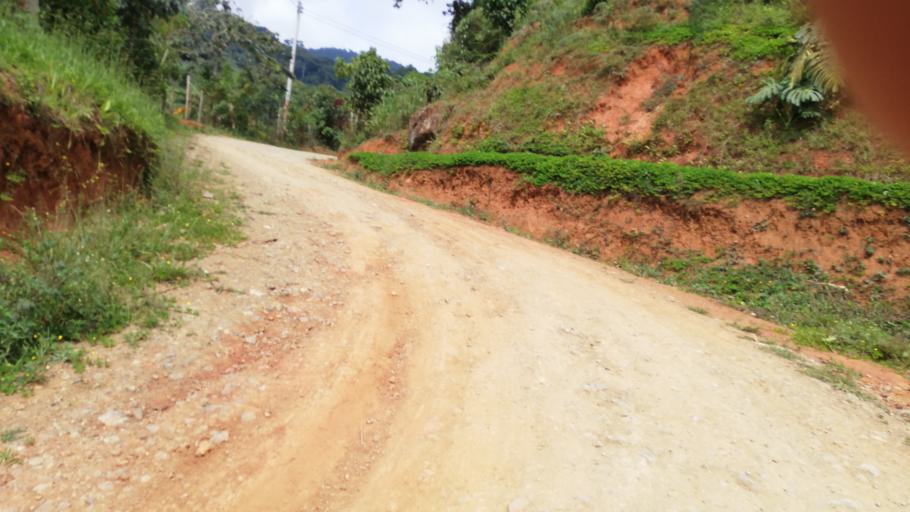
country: CO
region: Valle del Cauca
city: Yumbo
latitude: 3.6280
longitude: -76.5451
